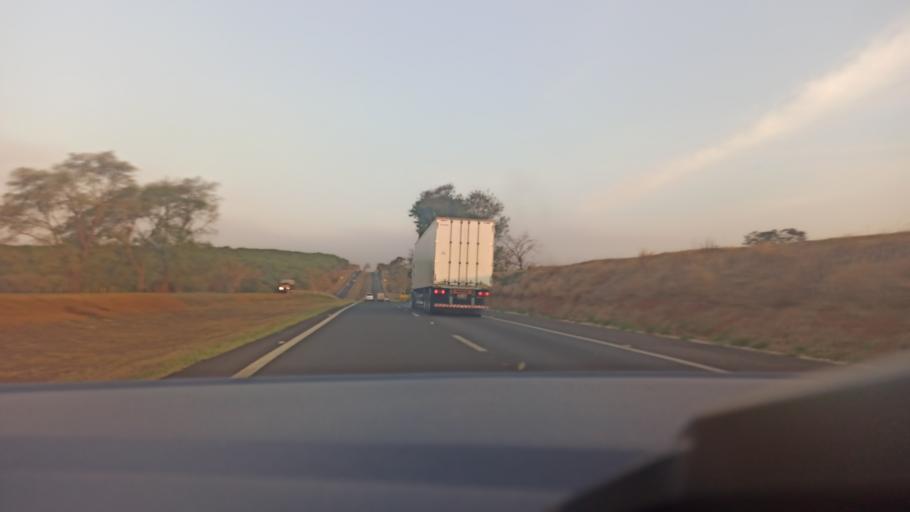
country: BR
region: Sao Paulo
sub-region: Taquaritinga
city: Taquaritinga
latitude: -21.4480
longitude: -48.6386
